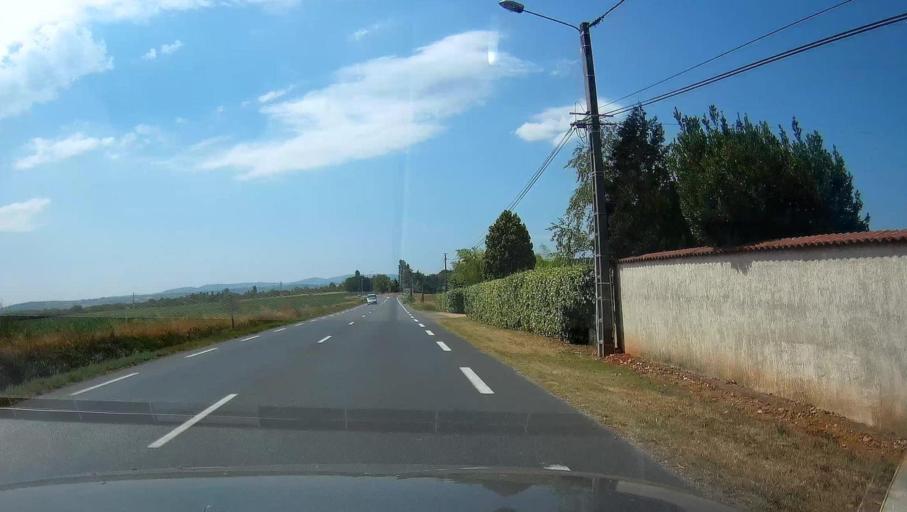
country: FR
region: Rhone-Alpes
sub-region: Departement de l'Ain
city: Reyrieux
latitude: 45.9309
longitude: 4.8044
